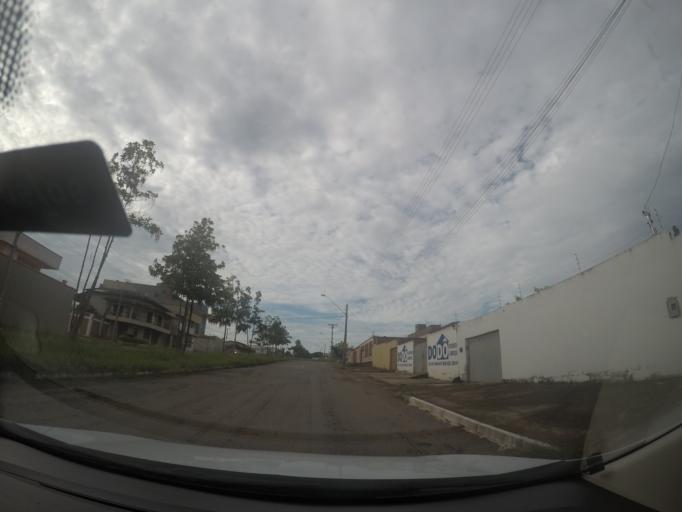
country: BR
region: Goias
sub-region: Goiania
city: Goiania
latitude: -16.6778
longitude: -49.2026
